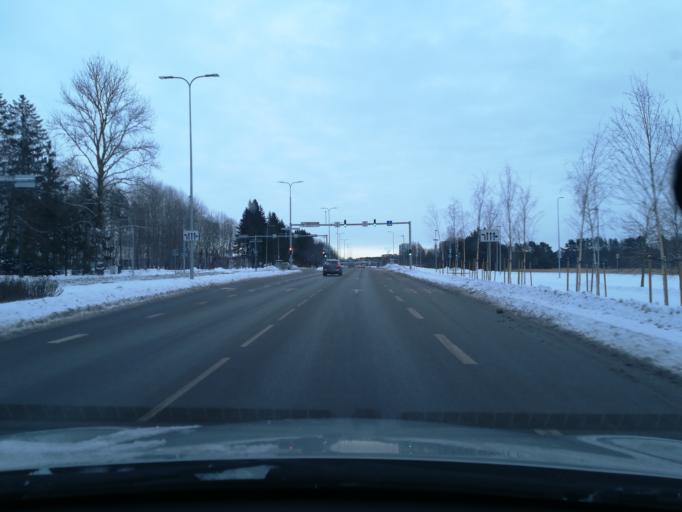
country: EE
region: Harju
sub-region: Saue vald
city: Laagri
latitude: 59.4270
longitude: 24.6300
